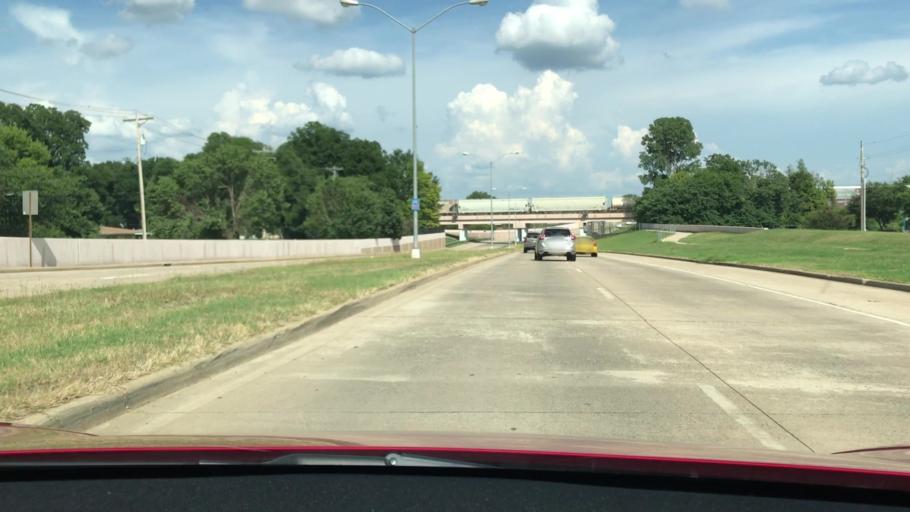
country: US
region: Louisiana
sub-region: Bossier Parish
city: Bossier City
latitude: 32.5118
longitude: -93.7255
